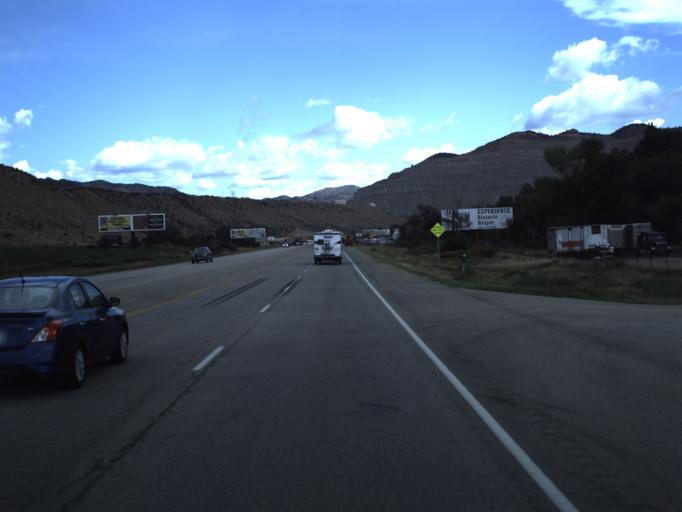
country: US
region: Utah
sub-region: Carbon County
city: Spring Glen
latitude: 39.6629
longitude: -110.8609
